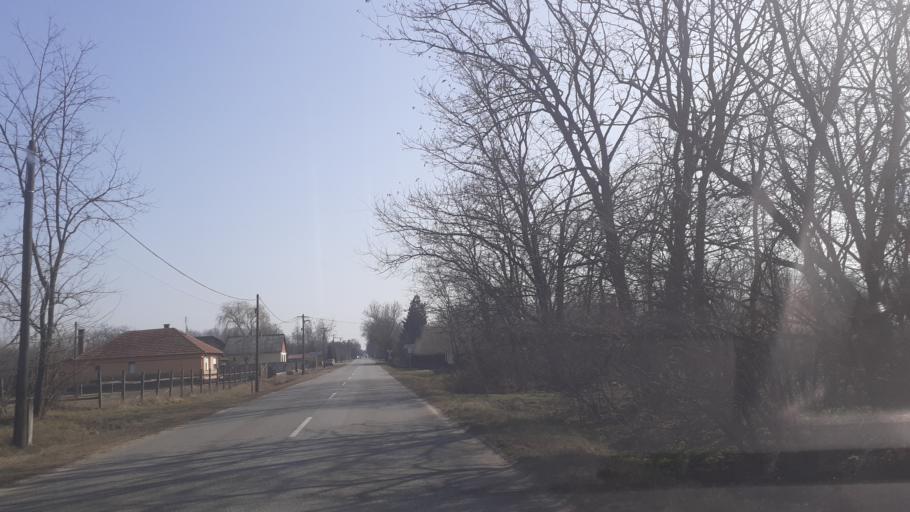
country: HU
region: Pest
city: Taborfalva
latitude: 47.0387
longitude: 19.4443
